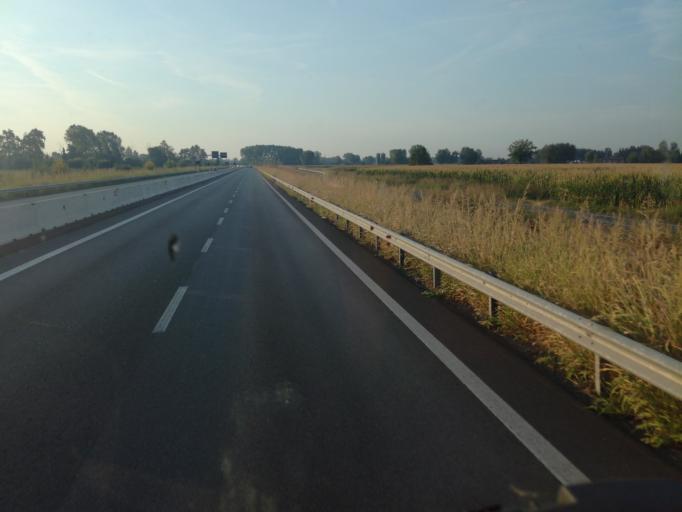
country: IT
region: Lombardy
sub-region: Provincia di Cremona
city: Spino d'Adda
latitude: 45.3985
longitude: 9.4758
